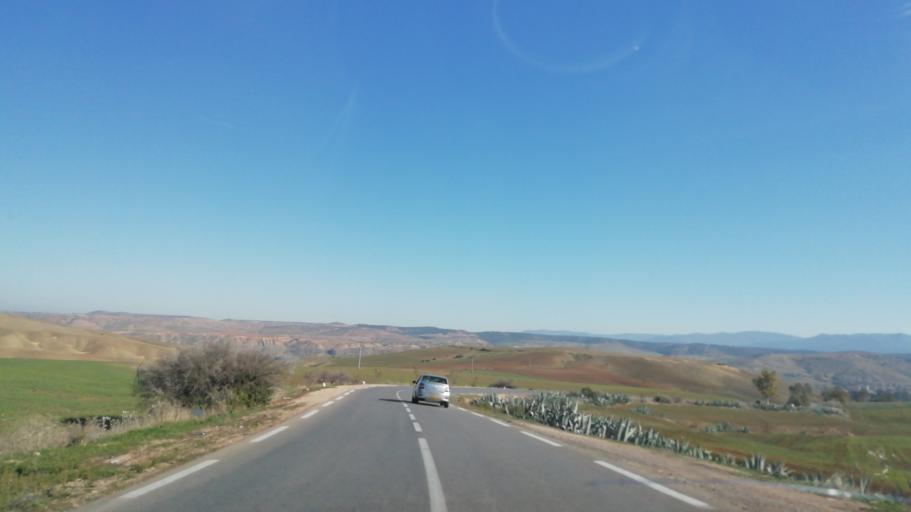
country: DZ
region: Tlemcen
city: Nedroma
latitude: 34.8313
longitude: -1.6709
